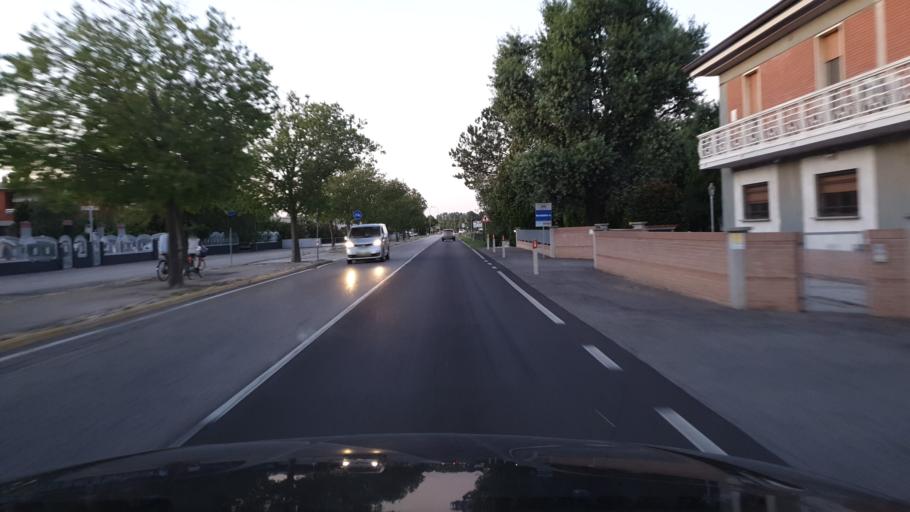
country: IT
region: Emilia-Romagna
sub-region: Provincia di Bologna
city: Altedo
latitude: 44.6738
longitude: 11.4911
